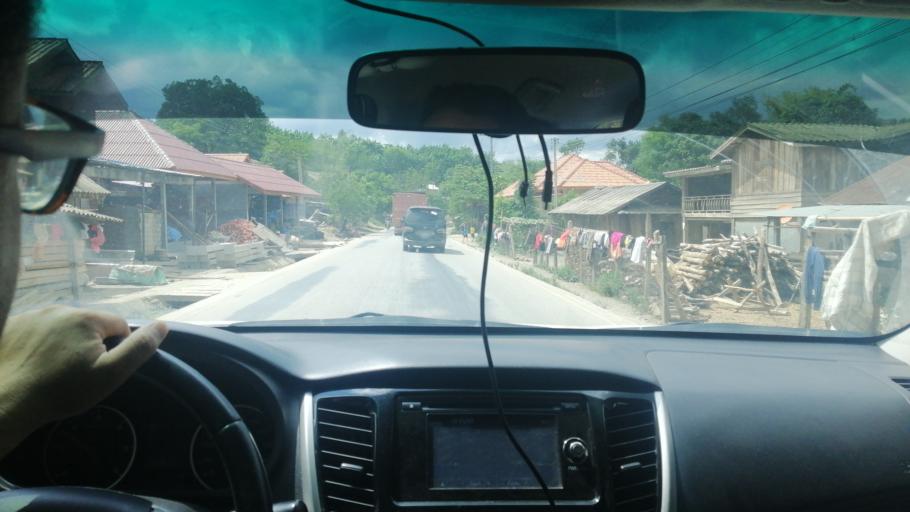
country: LA
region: Loungnamtha
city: Louang Namtha
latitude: 21.0375
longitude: 101.6501
